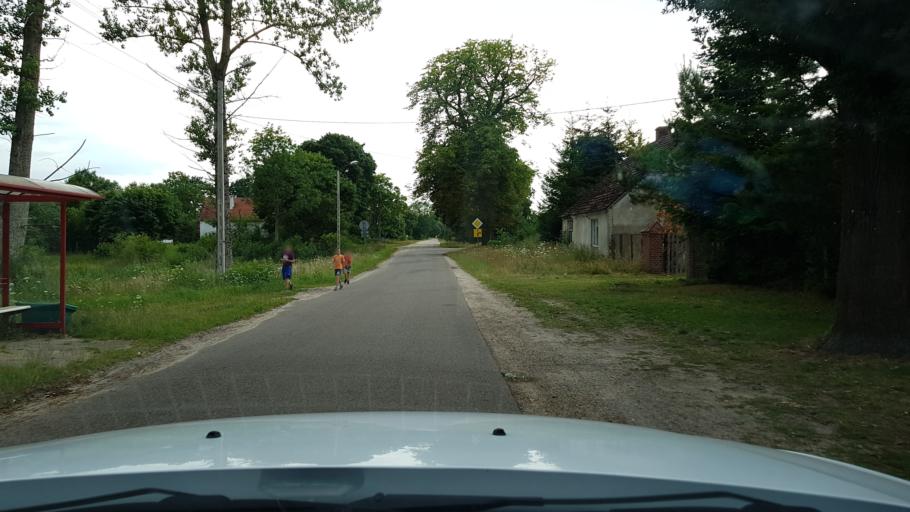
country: PL
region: West Pomeranian Voivodeship
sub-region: Powiat drawski
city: Czaplinek
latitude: 53.4251
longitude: 16.3178
